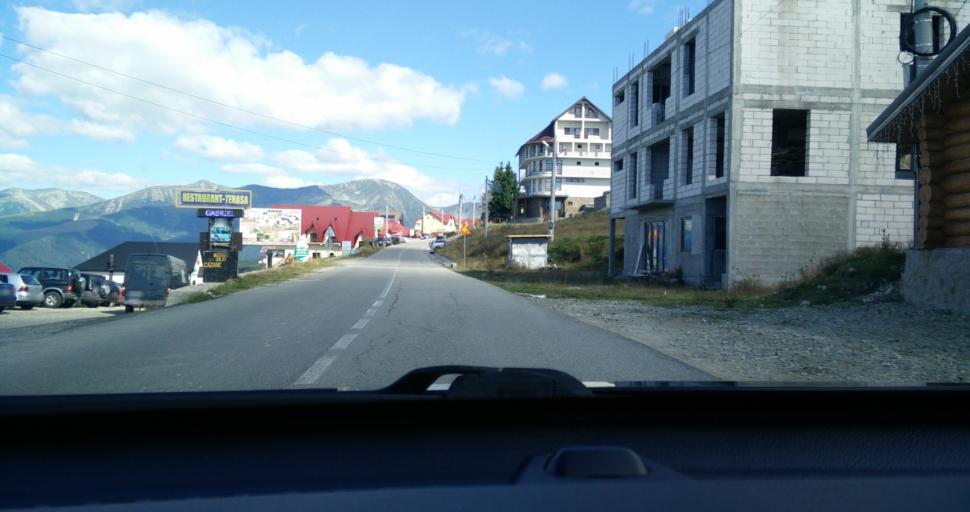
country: RO
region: Gorj
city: Novaci-Straini
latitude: 45.2762
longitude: 23.6899
